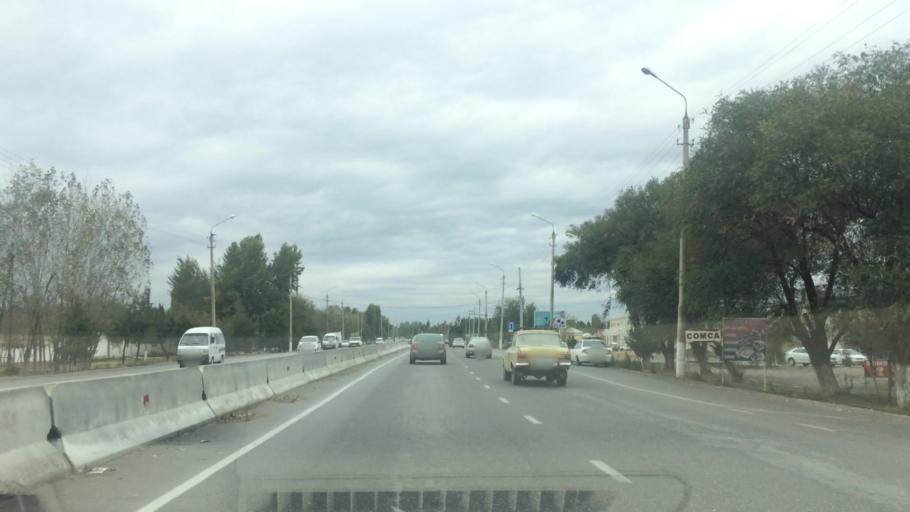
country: UZ
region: Jizzax
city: Jizzax
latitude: 39.9996
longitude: 67.5903
